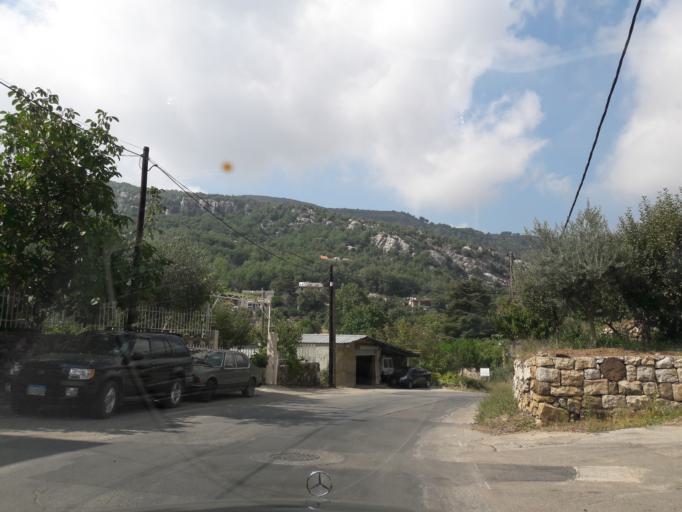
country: LB
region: Mont-Liban
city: Djounie
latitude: 33.9620
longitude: 35.7800
